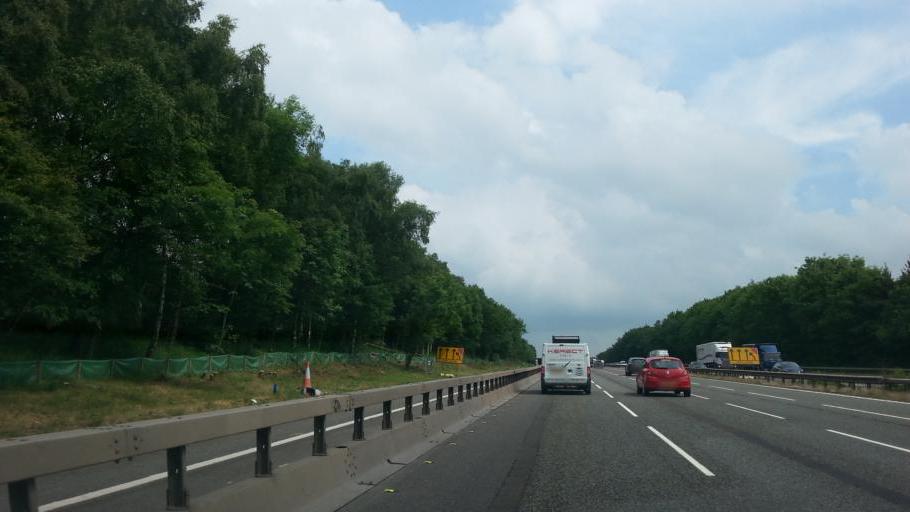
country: GB
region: England
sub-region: Solihull
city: Meriden
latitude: 52.4682
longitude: -1.6269
